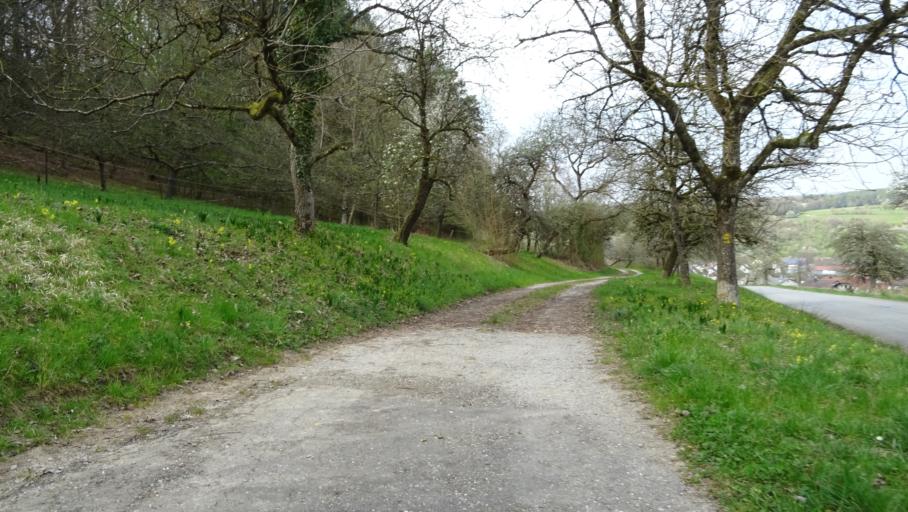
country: DE
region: Baden-Wuerttemberg
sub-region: Karlsruhe Region
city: Mosbach
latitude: 49.3722
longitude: 9.1728
